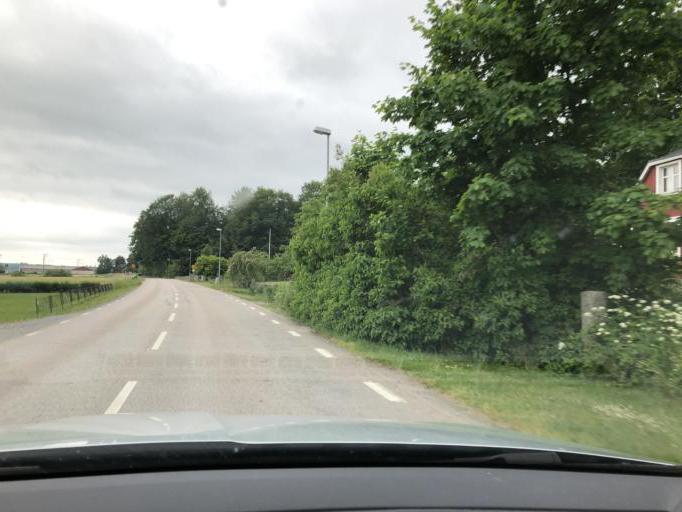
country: SE
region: Blekinge
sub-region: Solvesborgs Kommun
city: Soelvesborg
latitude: 56.1010
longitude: 14.6173
